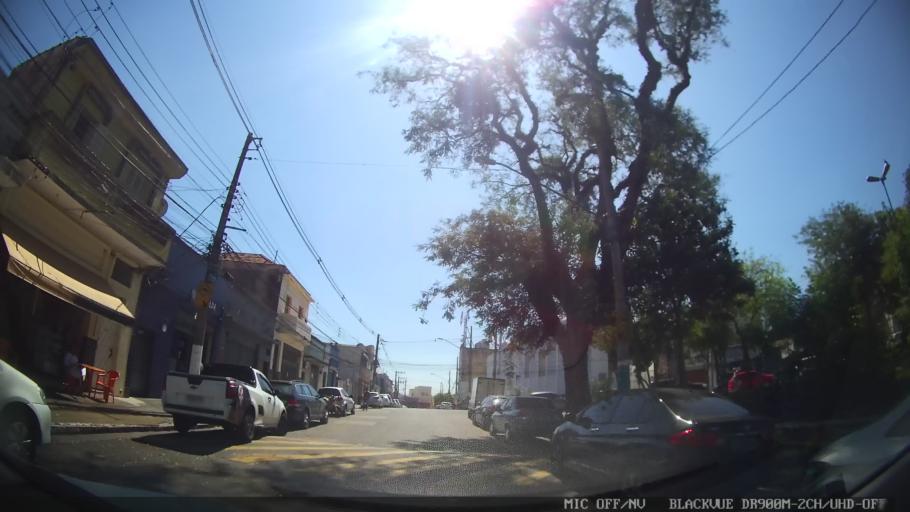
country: BR
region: Sao Paulo
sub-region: Sao Paulo
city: Sao Paulo
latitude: -23.5090
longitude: -46.6573
